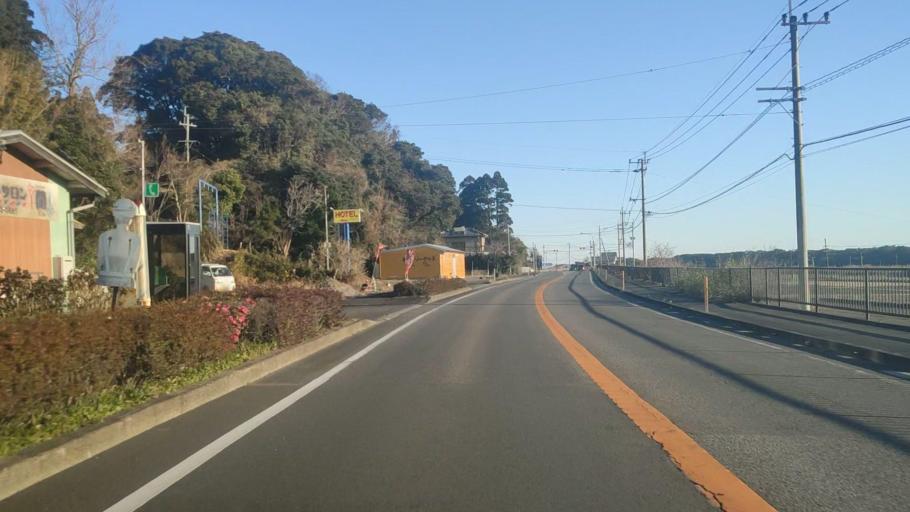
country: JP
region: Miyazaki
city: Takanabe
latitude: 32.0941
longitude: 131.5161
